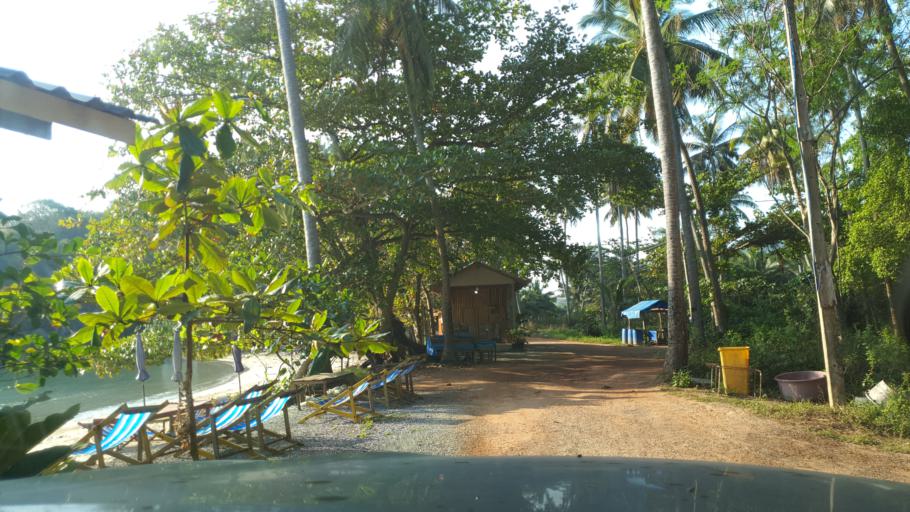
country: TH
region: Prachuap Khiri Khan
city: Bang Saphan
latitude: 11.2116
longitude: 99.5791
